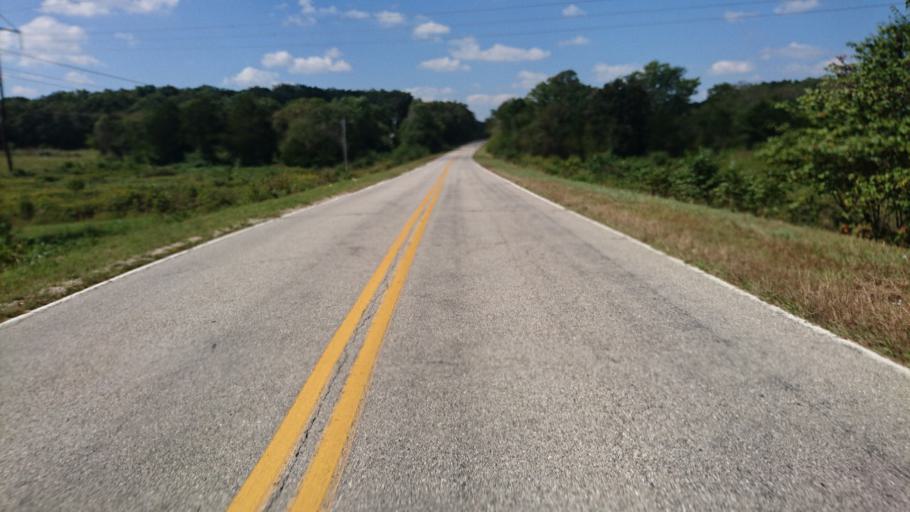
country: US
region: Missouri
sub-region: Pulaski County
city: Richland
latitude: 37.7523
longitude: -92.4923
